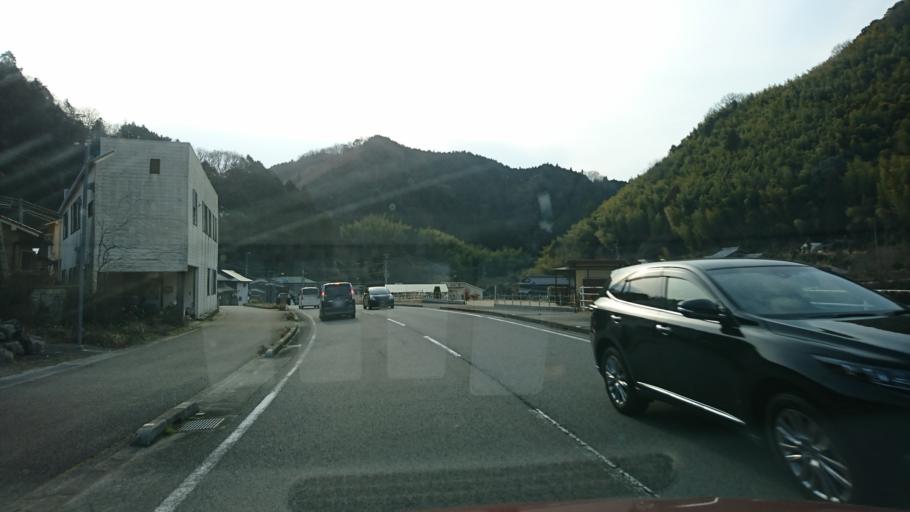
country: JP
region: Ehime
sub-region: Shikoku-chuo Shi
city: Matsuyama
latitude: 33.8980
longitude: 132.8613
